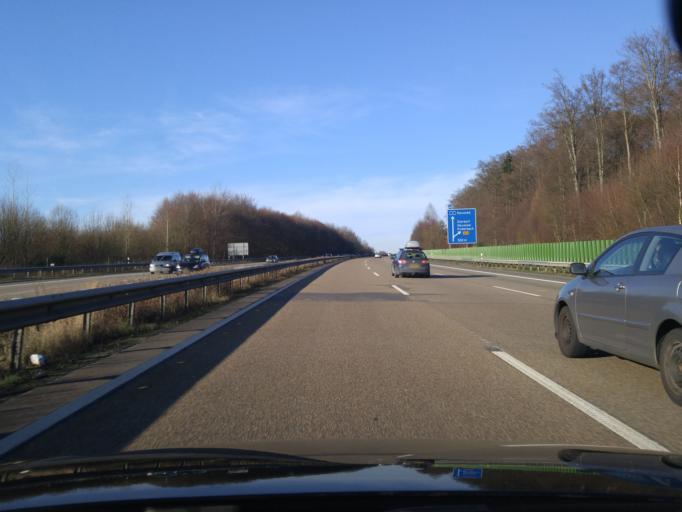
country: DE
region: Rheinland-Pfalz
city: Kleinmaischeid
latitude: 50.5287
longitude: 7.6077
